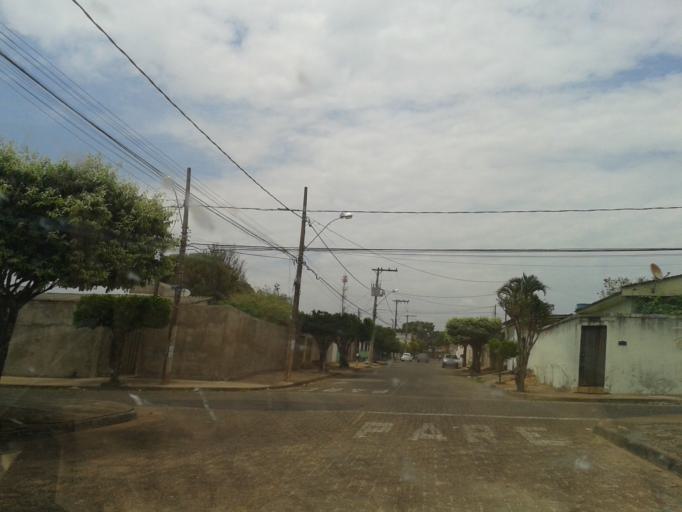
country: BR
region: Minas Gerais
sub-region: Uberlandia
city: Uberlandia
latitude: -18.9336
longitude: -48.3016
